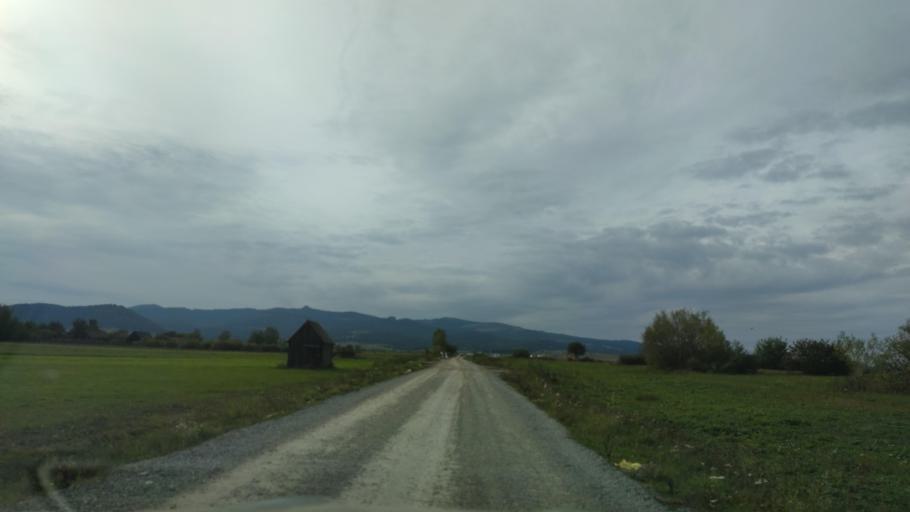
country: RO
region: Harghita
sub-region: Comuna Remetea
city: Remetea
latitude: 46.8165
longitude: 25.4184
